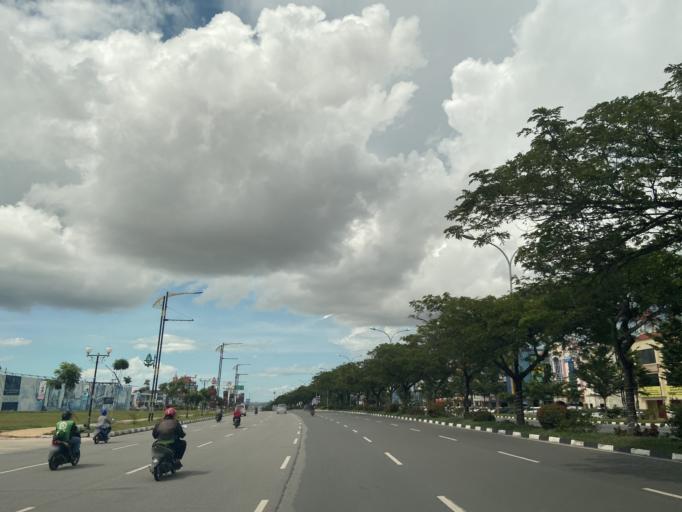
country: SG
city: Singapore
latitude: 1.1251
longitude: 104.0282
